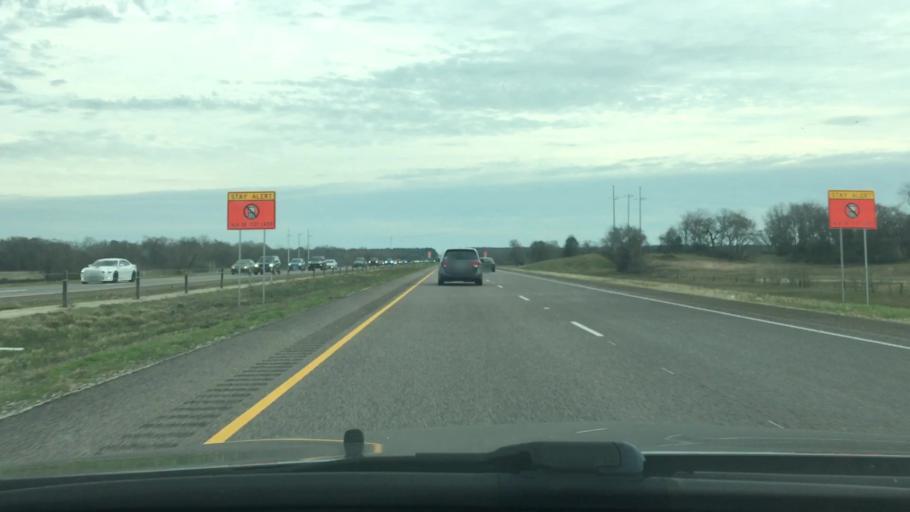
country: US
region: Texas
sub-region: Madison County
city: Madisonville
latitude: 30.9017
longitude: -95.7832
